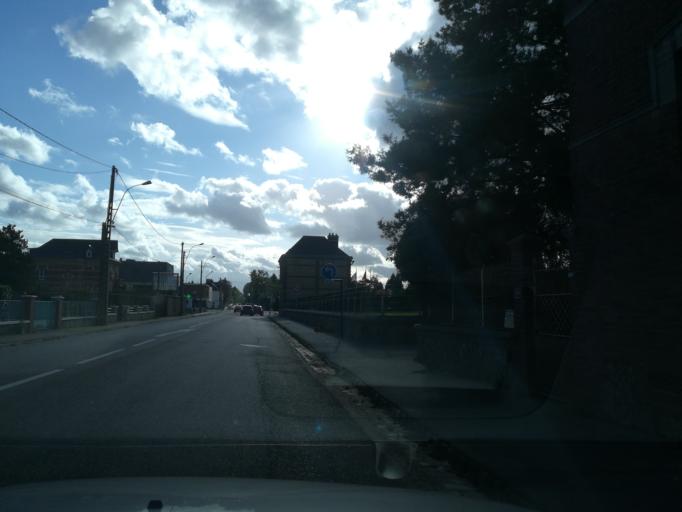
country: FR
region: Haute-Normandie
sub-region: Departement de la Seine-Maritime
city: Bois-Guillaume
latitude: 49.4710
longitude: 1.1211
